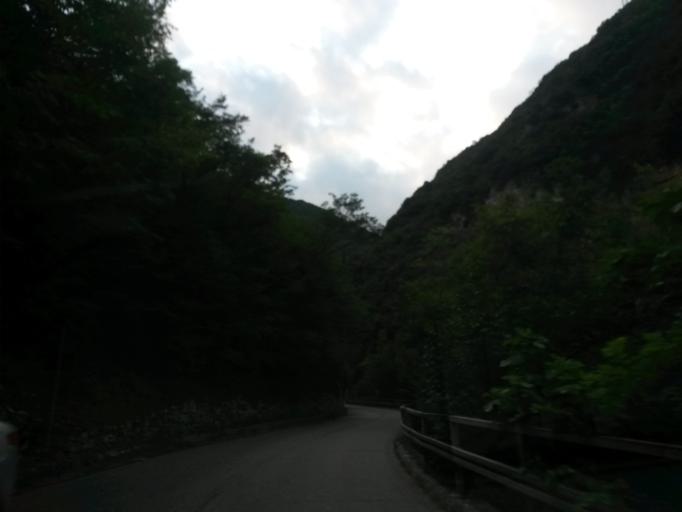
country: IT
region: Lombardy
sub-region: Provincia di Brescia
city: Gardola
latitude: 45.7305
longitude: 10.7073
